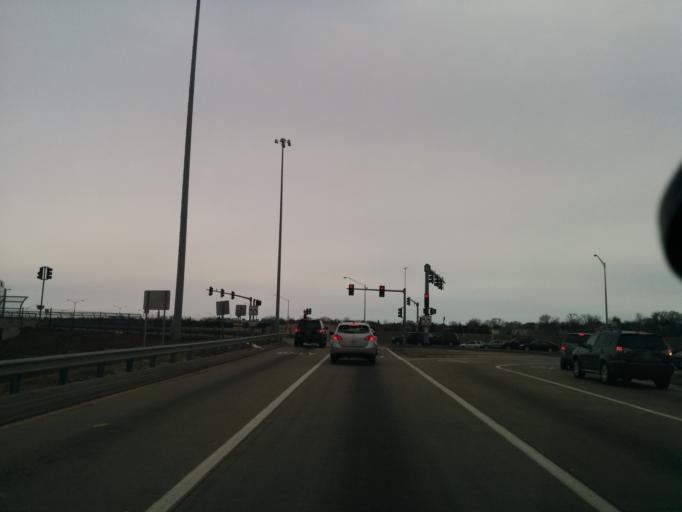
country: US
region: Illinois
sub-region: Cook County
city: Northbrook
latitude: 42.1057
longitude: -87.8673
